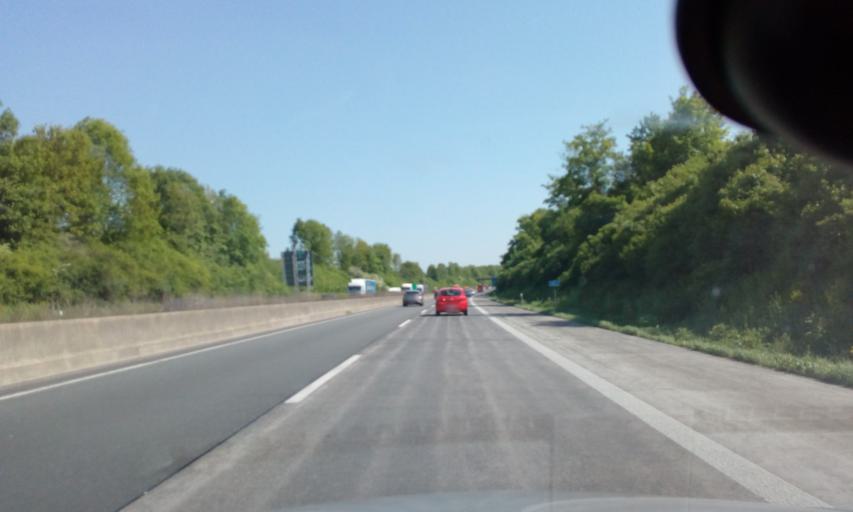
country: DE
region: North Rhine-Westphalia
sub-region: Regierungsbezirk Koln
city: Bergheim
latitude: 50.9337
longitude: 6.6595
